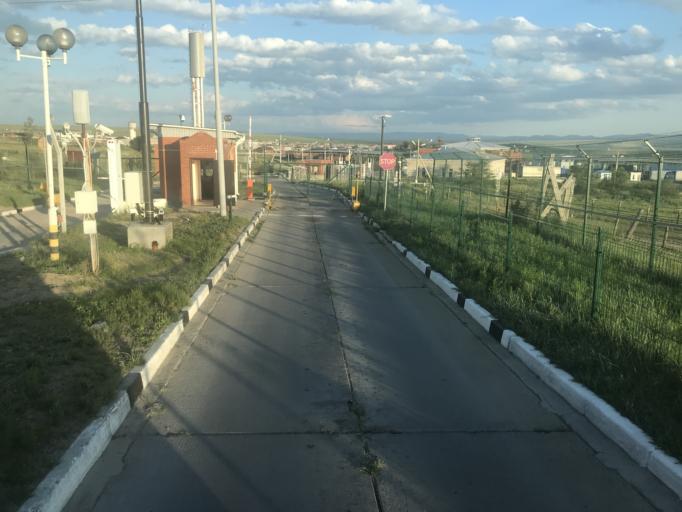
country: MN
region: Selenge
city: Altanbulag
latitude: 50.3240
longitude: 106.4886
